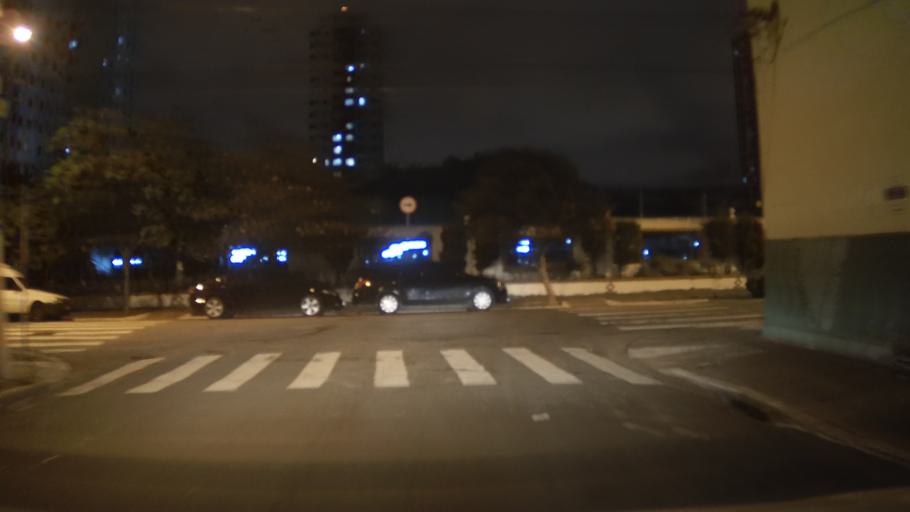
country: BR
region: Sao Paulo
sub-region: Sao Paulo
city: Sao Paulo
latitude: -23.5497
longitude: -46.6196
